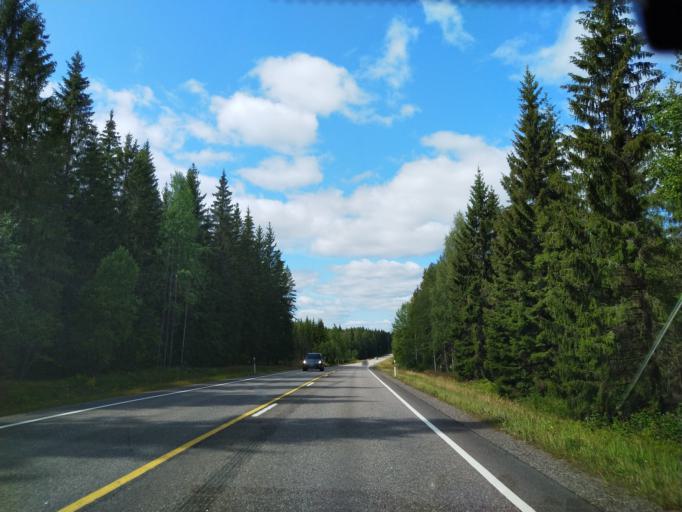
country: FI
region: Haeme
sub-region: Haemeenlinna
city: Renko
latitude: 60.7663
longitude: 24.2489
